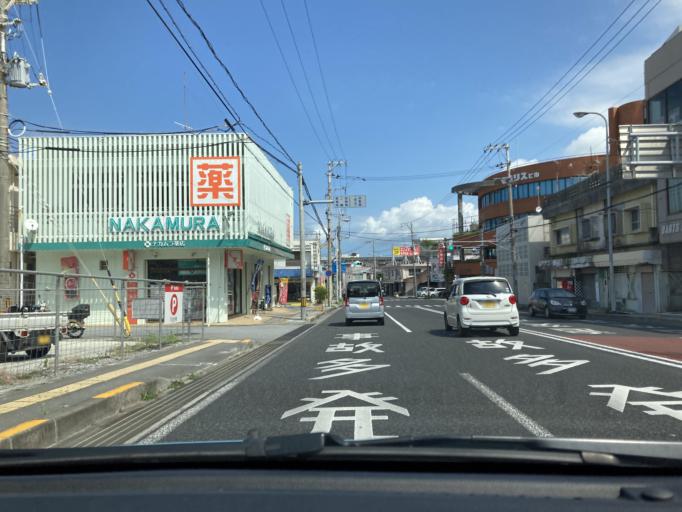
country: JP
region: Okinawa
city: Chatan
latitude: 26.2884
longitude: 127.7776
